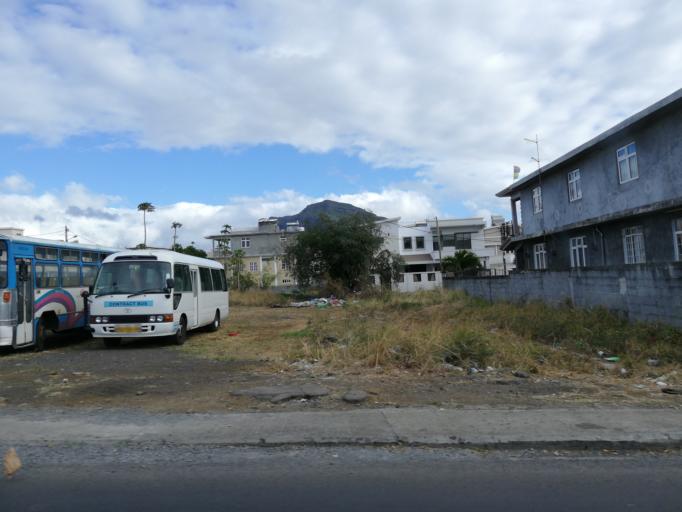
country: MU
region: Black River
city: Gros Cailloux
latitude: -20.2311
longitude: 57.4533
